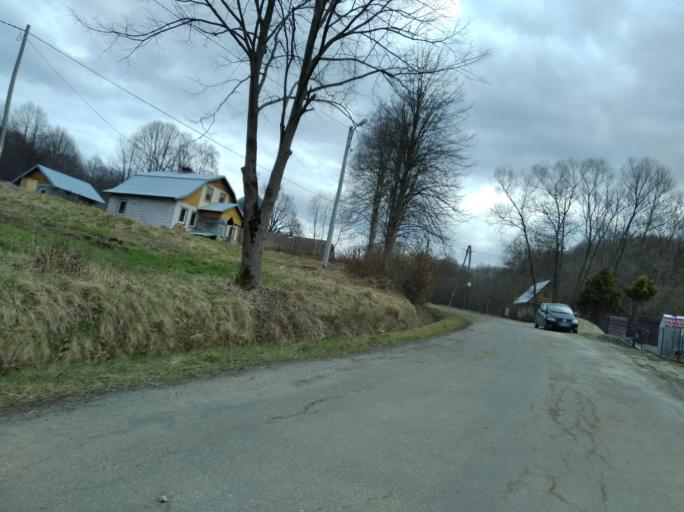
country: PL
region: Subcarpathian Voivodeship
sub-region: Powiat strzyzowski
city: Wysoka Strzyzowska
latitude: 49.7907
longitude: 21.7249
